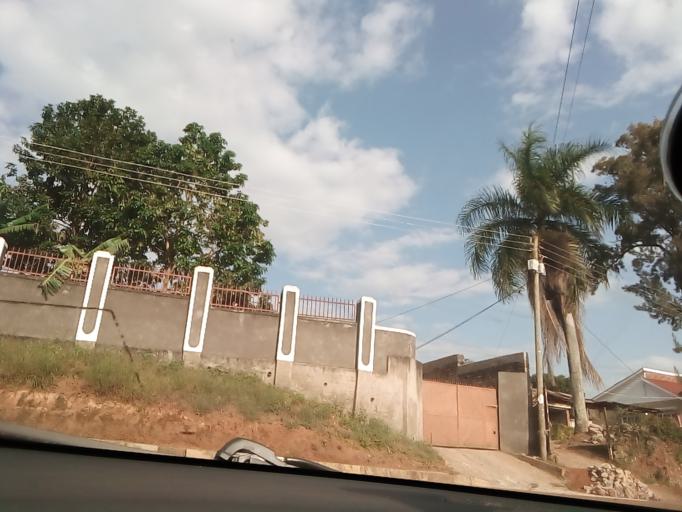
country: UG
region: Central Region
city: Masaka
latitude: -0.3508
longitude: 31.7429
